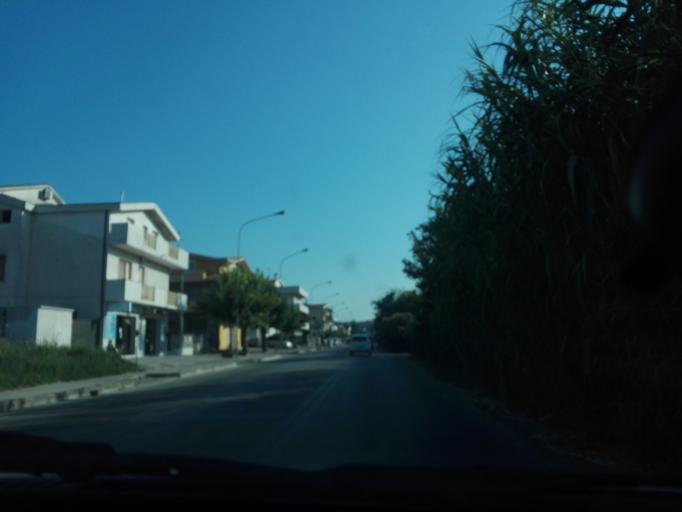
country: IT
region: Abruzzo
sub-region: Provincia di Pescara
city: Cappelle sul Tavo
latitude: 42.4859
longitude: 14.1188
